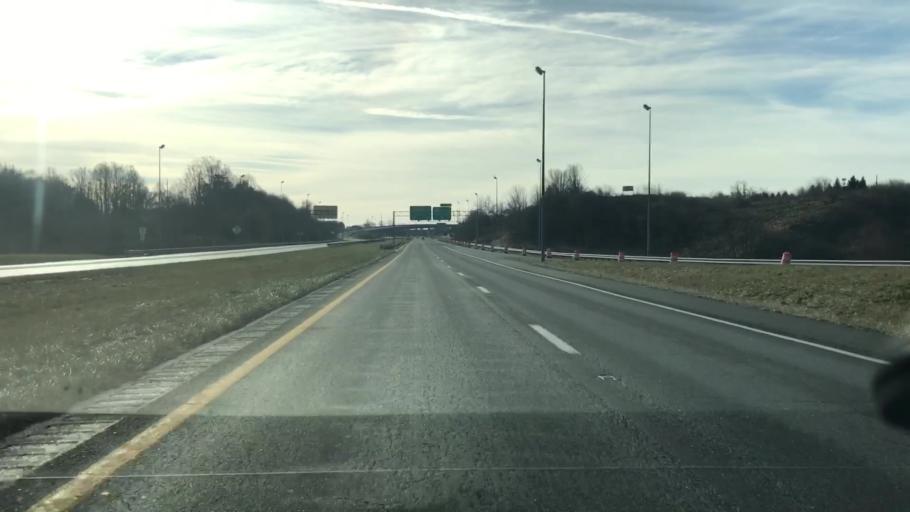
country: US
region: Virginia
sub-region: Montgomery County
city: Merrimac
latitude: 37.1626
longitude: -80.4142
